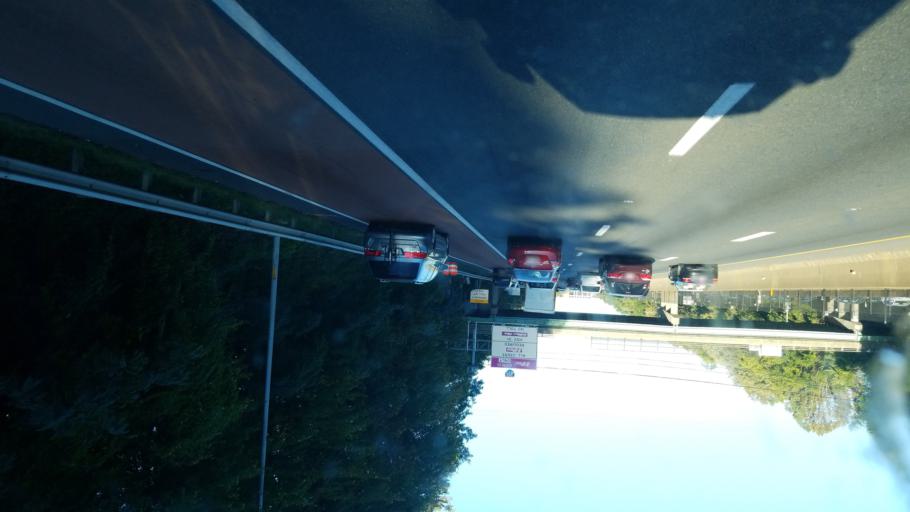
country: US
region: Virginia
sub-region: Fairfax County
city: Merrifield
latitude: 38.8794
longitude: -77.2481
